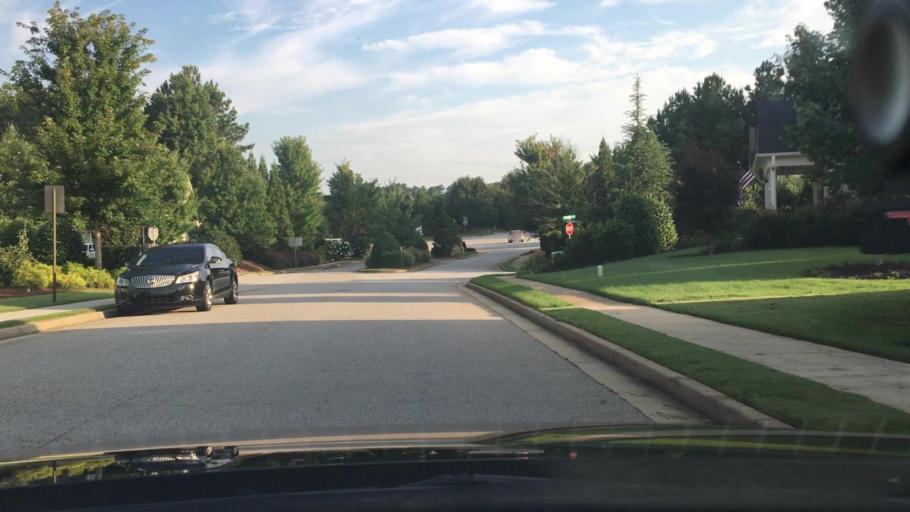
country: US
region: Georgia
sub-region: Coweta County
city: East Newnan
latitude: 33.3855
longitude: -84.7500
